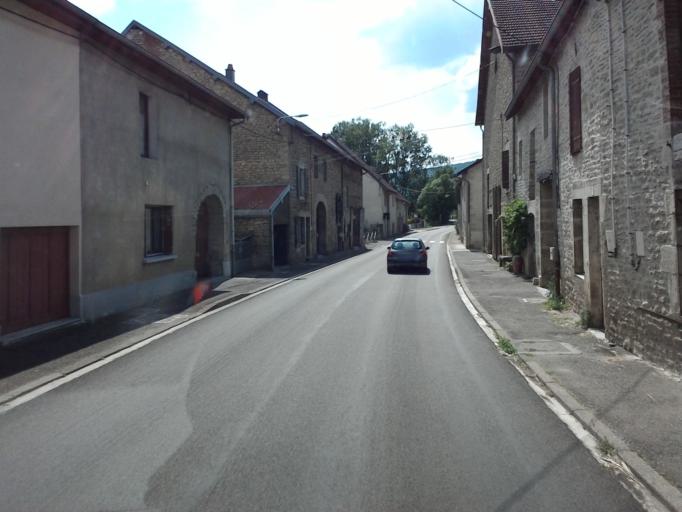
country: FR
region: Franche-Comte
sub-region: Departement du Doubs
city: Quingey
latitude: 47.1063
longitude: 5.8919
